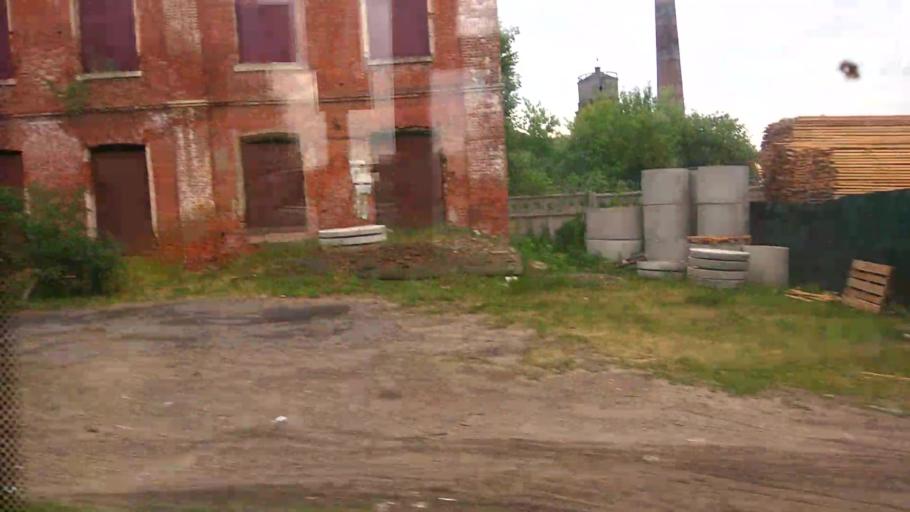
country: RU
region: Moskovskaya
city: Ozery
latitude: 54.8523
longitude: 38.5695
